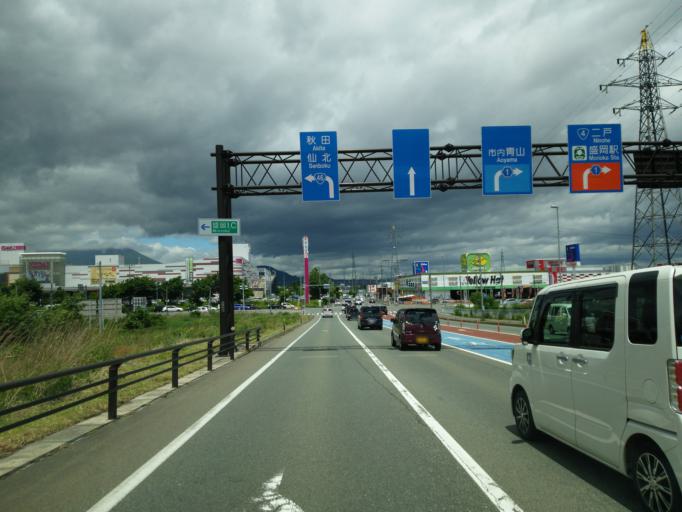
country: JP
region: Iwate
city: Morioka-shi
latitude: 39.7092
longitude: 141.1013
